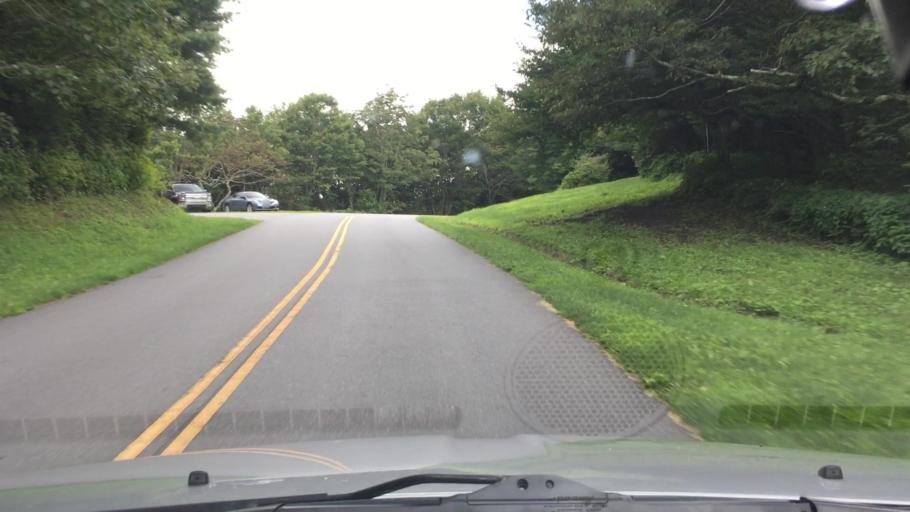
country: US
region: North Carolina
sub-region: Buncombe County
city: Swannanoa
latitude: 35.6996
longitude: -82.3991
